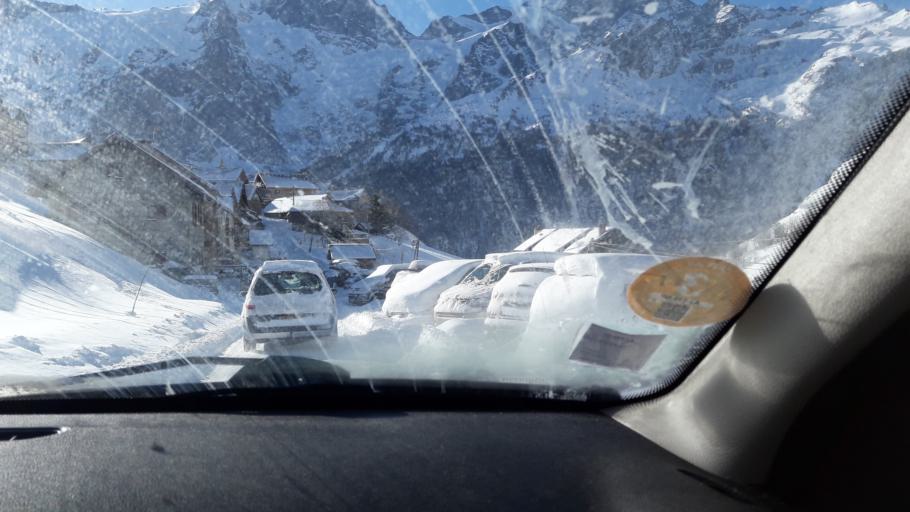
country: FR
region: Rhone-Alpes
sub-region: Departement de l'Isere
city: Mont-de-Lans
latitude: 45.0557
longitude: 6.2834
